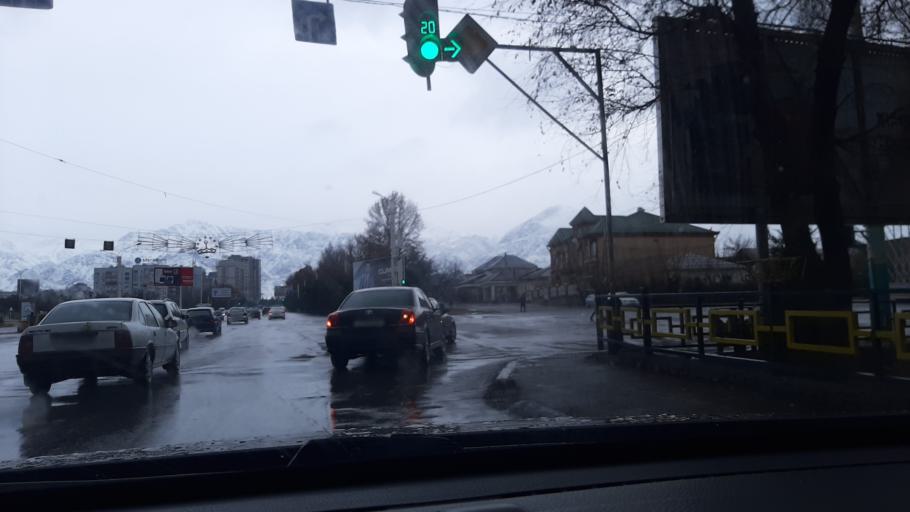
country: TJ
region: Viloyati Sughd
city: Khujand
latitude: 40.2941
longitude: 69.6180
